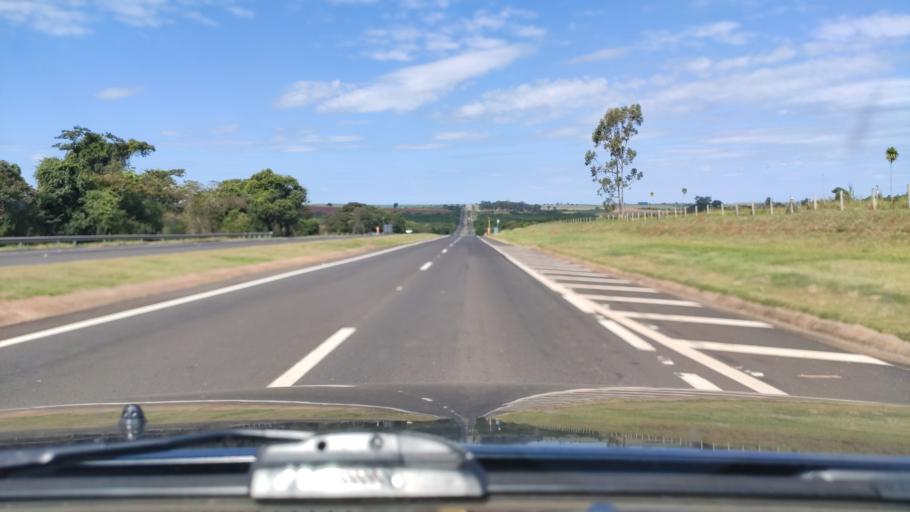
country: BR
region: Sao Paulo
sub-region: Rancharia
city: Rancharia
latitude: -22.4834
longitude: -50.9258
